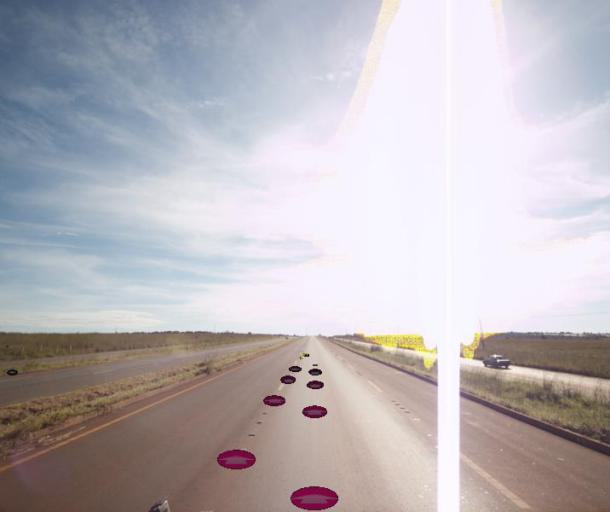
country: BR
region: Federal District
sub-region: Brasilia
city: Brasilia
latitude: -15.7481
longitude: -48.3217
